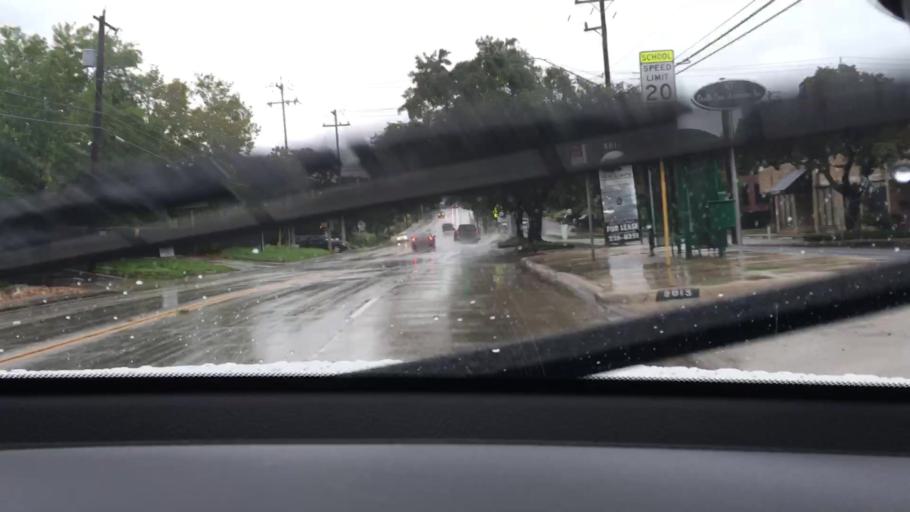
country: US
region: Texas
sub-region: Bexar County
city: Alamo Heights
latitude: 29.5081
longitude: -98.4663
